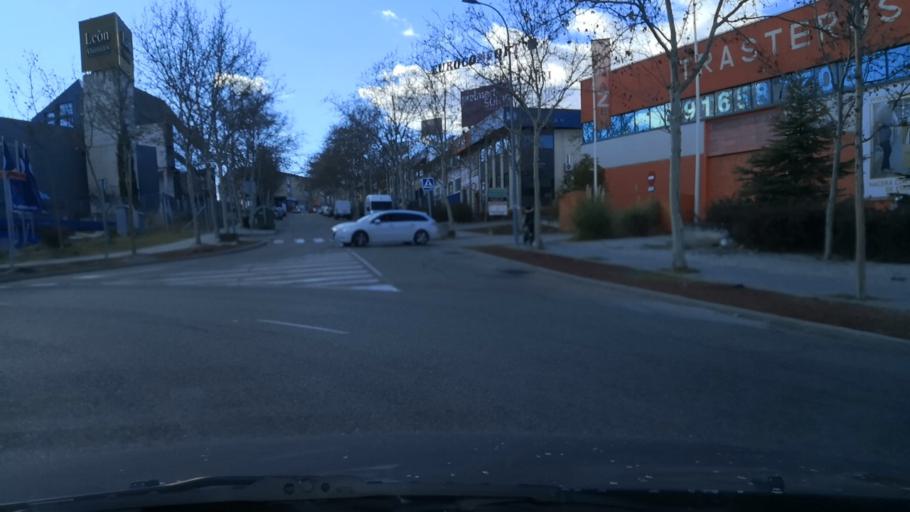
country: ES
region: Madrid
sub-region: Provincia de Madrid
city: San Sebastian de los Reyes
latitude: 40.5524
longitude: -3.6099
